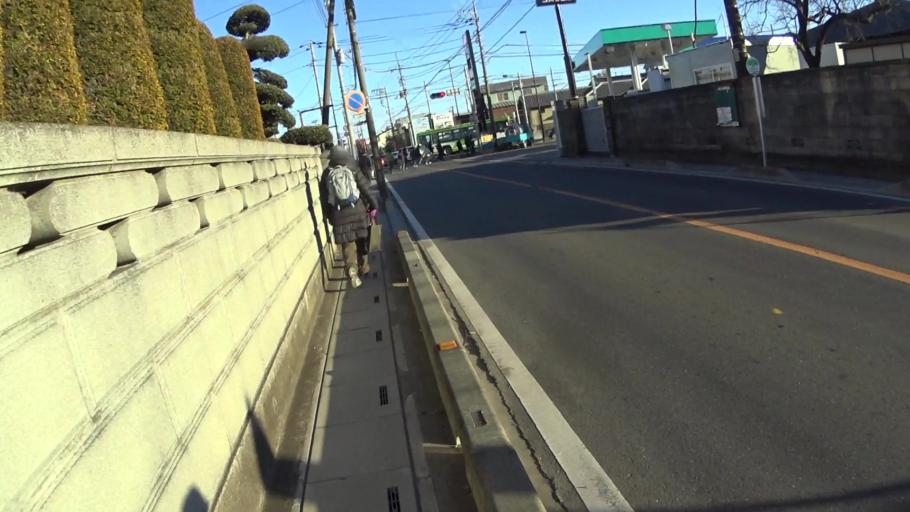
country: JP
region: Saitama
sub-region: Kawaguchi-shi
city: Hatogaya-honcho
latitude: 35.8859
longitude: 139.7261
